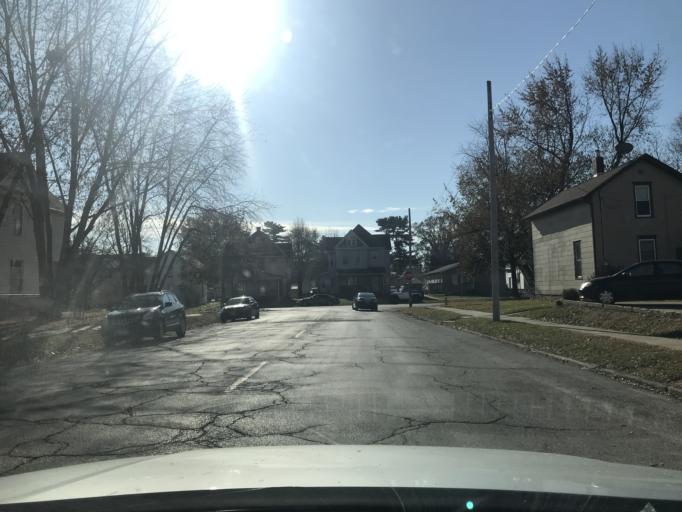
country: US
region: Iowa
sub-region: Scott County
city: Davenport
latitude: 41.5217
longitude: -90.6112
